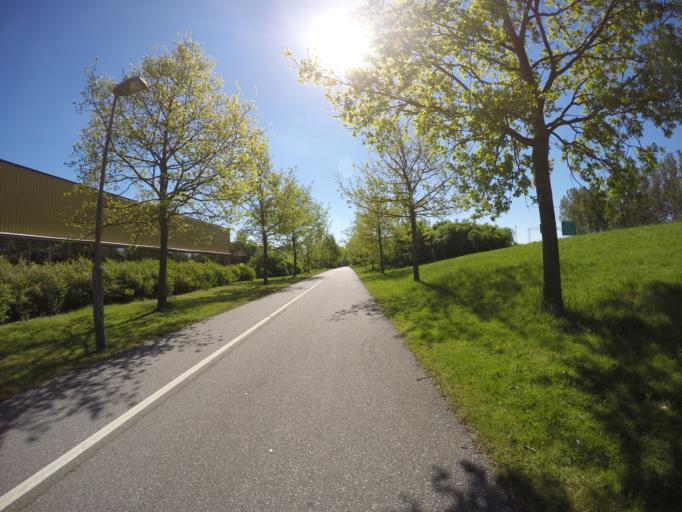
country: SE
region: Skane
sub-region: Malmo
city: Oxie
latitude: 55.5642
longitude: 13.0650
